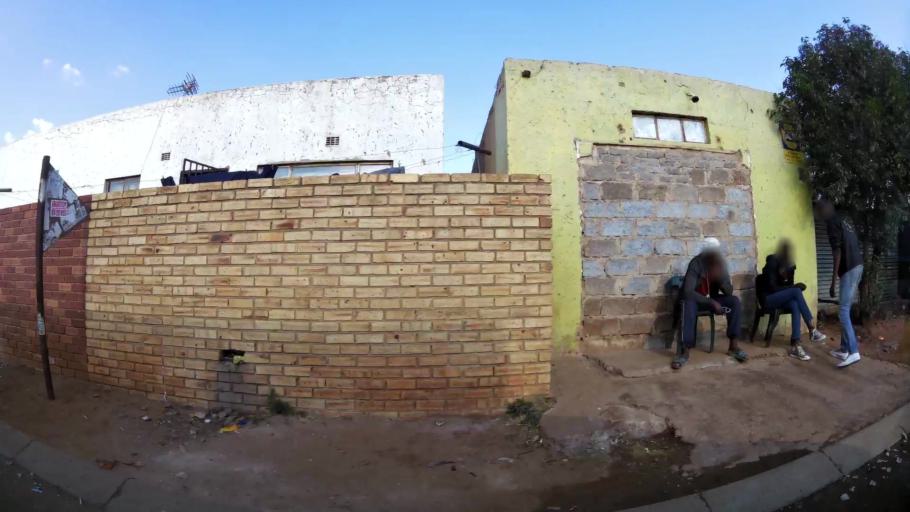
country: ZA
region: Gauteng
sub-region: Ekurhuleni Metropolitan Municipality
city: Tembisa
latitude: -25.9636
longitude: 28.2067
